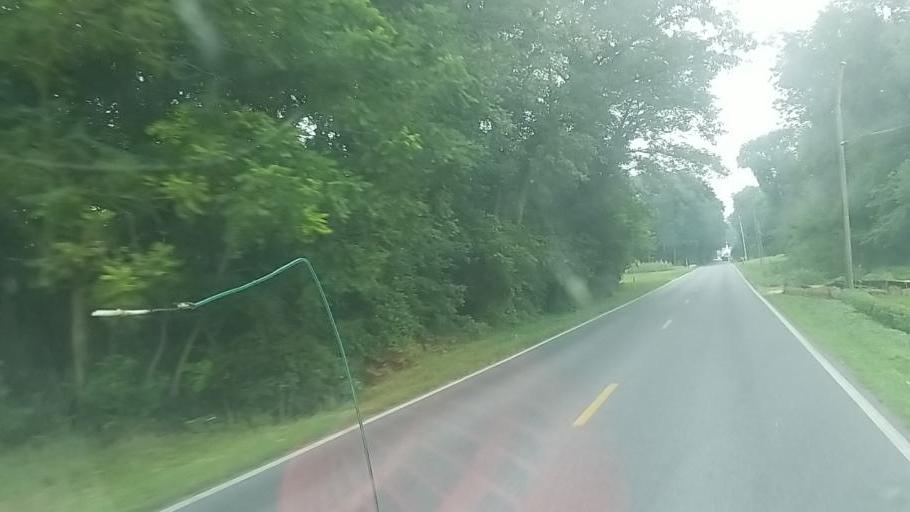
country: US
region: Maryland
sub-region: Wicomico County
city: Salisbury
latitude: 38.3948
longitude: -75.5317
